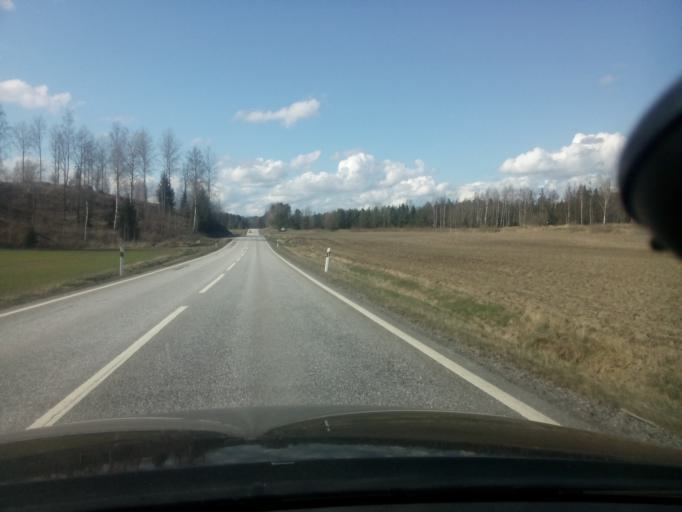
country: SE
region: Soedermanland
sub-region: Flens Kommun
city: Malmkoping
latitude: 59.1095
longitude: 16.7673
